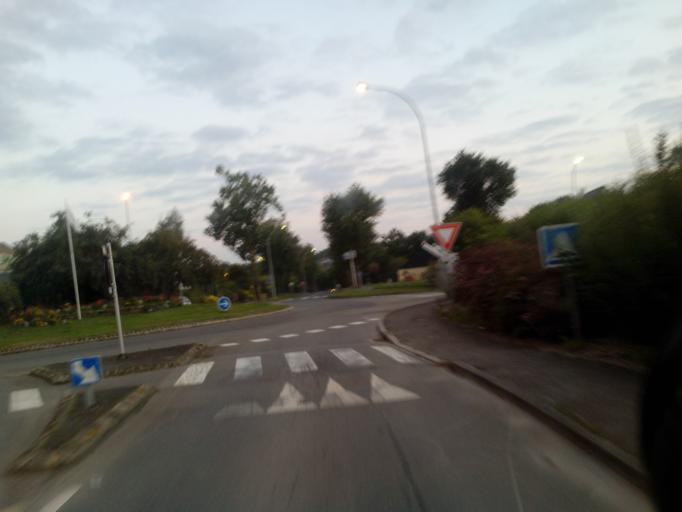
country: FR
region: Brittany
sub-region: Departement d'Ille-et-Vilaine
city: Montfort-sur-Meu
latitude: 48.1420
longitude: -1.9640
